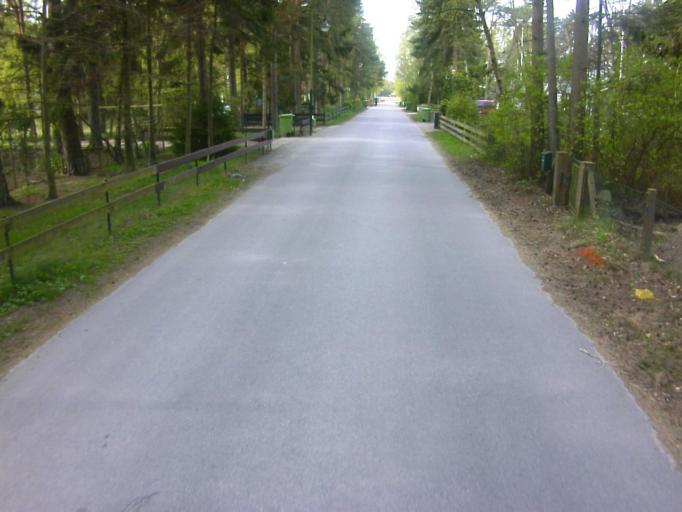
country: SE
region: Skane
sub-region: Kavlinge Kommun
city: Hofterup
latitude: 55.7591
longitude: 12.9819
